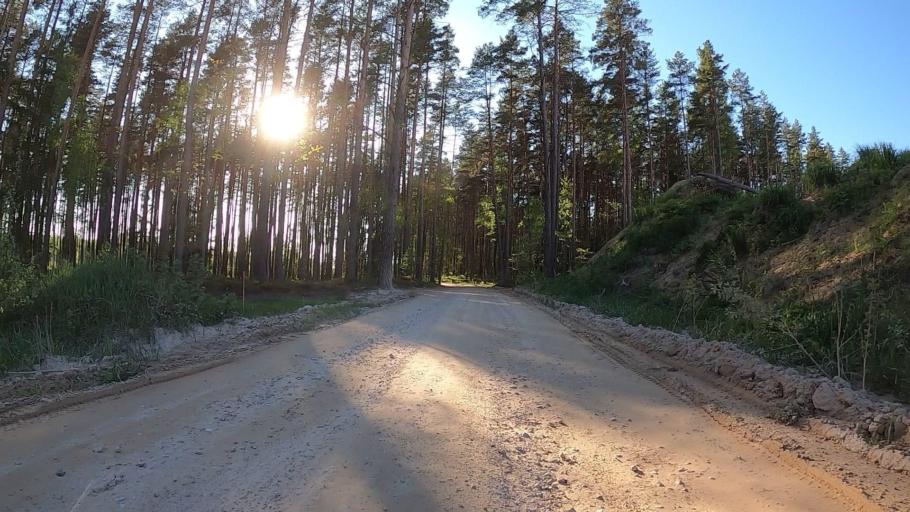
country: LV
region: Kekava
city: Kekava
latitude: 56.7817
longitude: 24.3071
